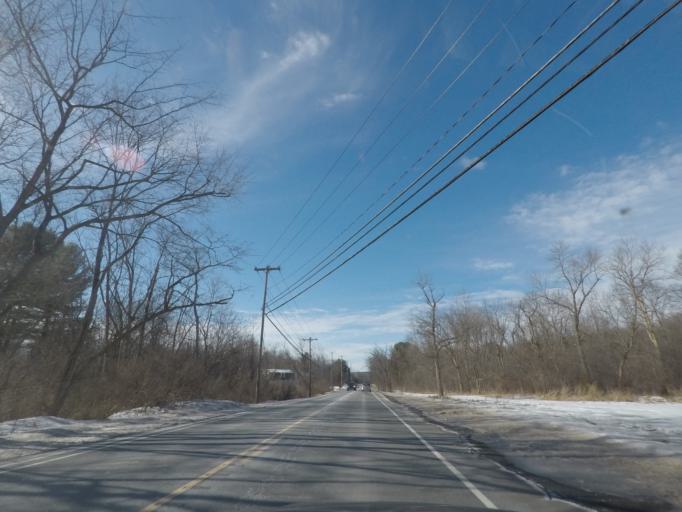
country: US
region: New York
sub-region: Albany County
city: Altamont
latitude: 42.7068
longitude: -73.9778
